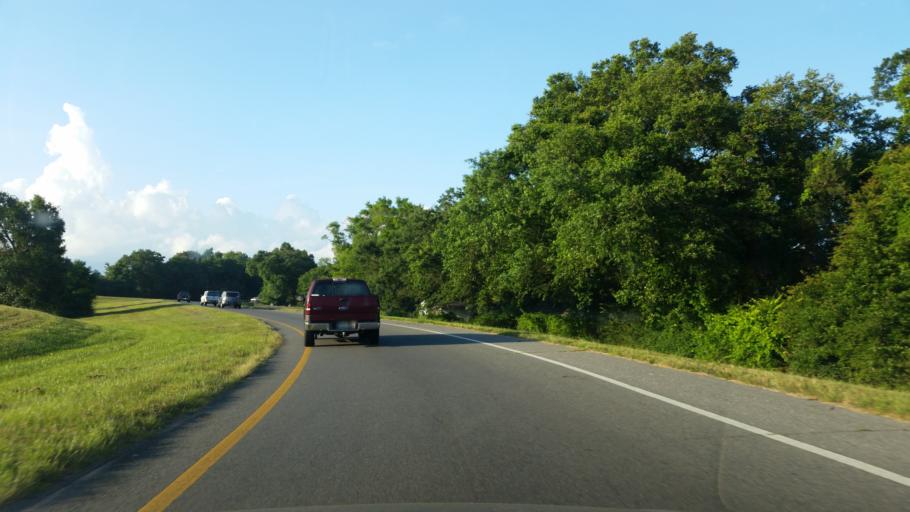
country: US
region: Florida
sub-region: Escambia County
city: West Pensacola
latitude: 30.4310
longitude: -87.2750
